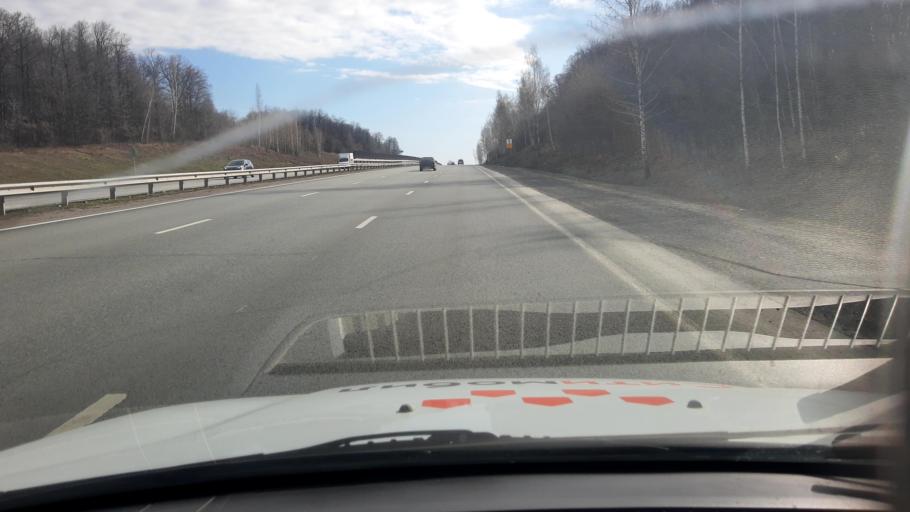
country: RU
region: Bashkortostan
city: Avdon
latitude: 54.6523
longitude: 55.6715
